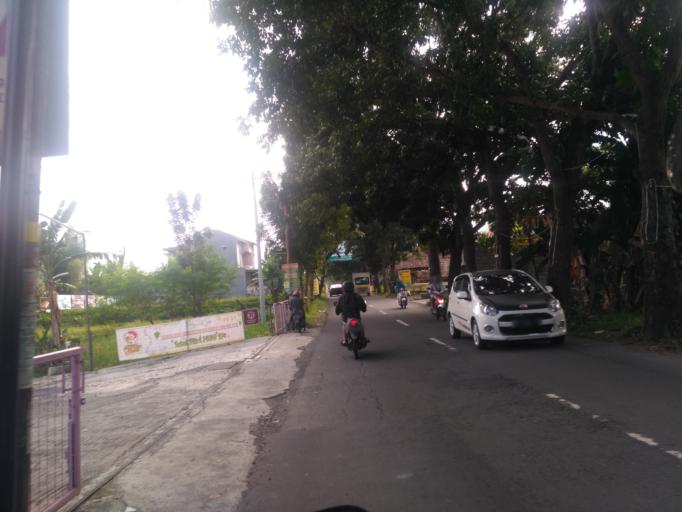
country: ID
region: Daerah Istimewa Yogyakarta
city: Yogyakarta
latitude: -7.7609
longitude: 110.3455
